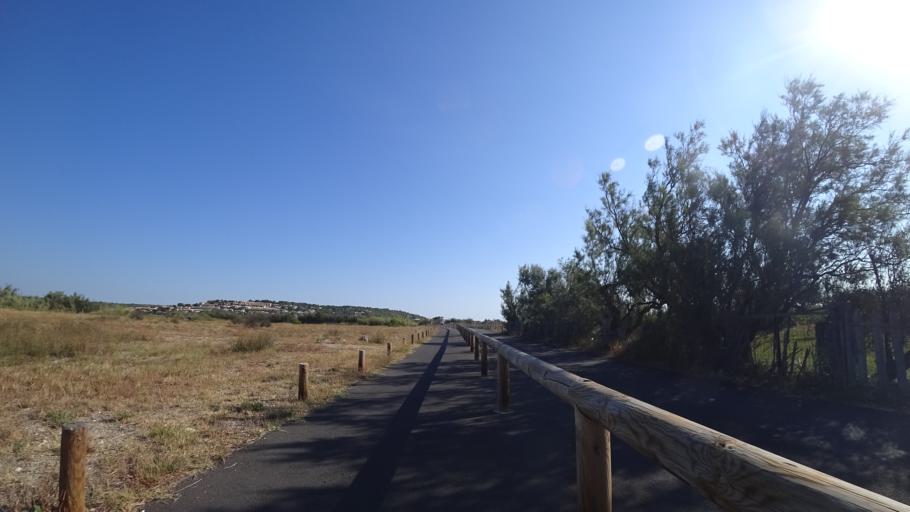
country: FR
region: Languedoc-Roussillon
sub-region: Departement de l'Aude
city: Leucate
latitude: 42.8953
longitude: 3.0513
